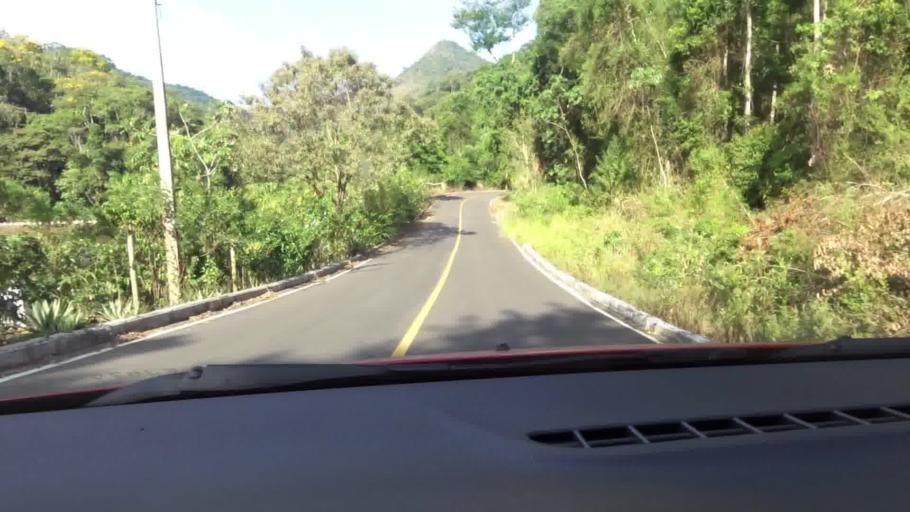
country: BR
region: Espirito Santo
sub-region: Guarapari
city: Guarapari
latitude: -20.5788
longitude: -40.5450
